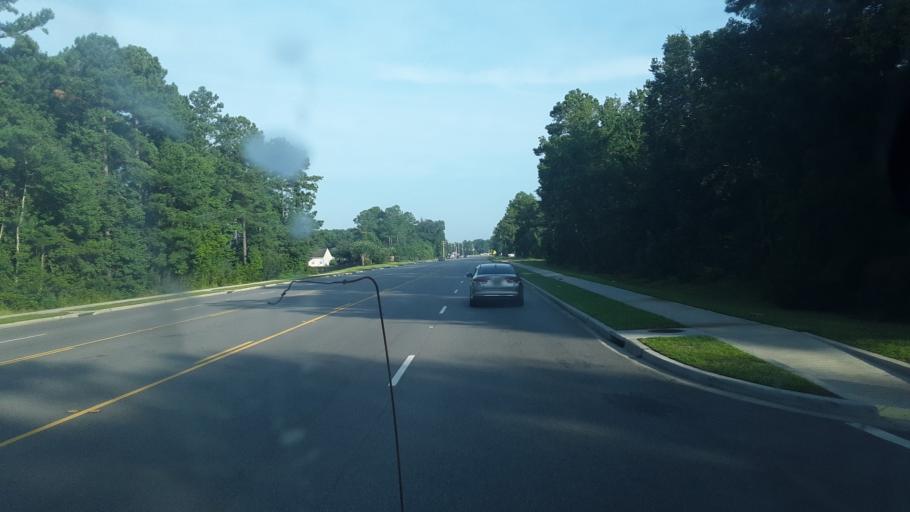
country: US
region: South Carolina
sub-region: Horry County
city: Myrtle Beach
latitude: 33.7619
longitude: -78.8605
